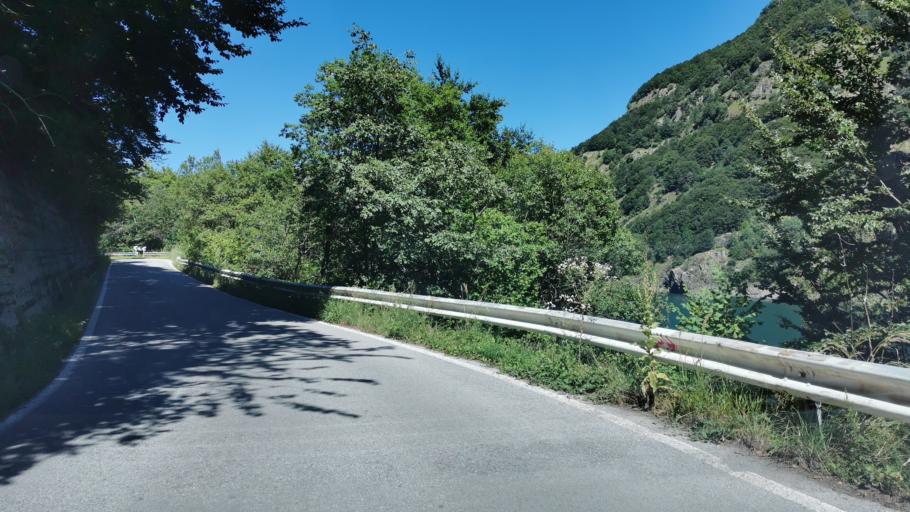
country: IT
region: Piedmont
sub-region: Provincia di Cuneo
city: Entracque
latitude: 44.2173
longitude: 7.3857
